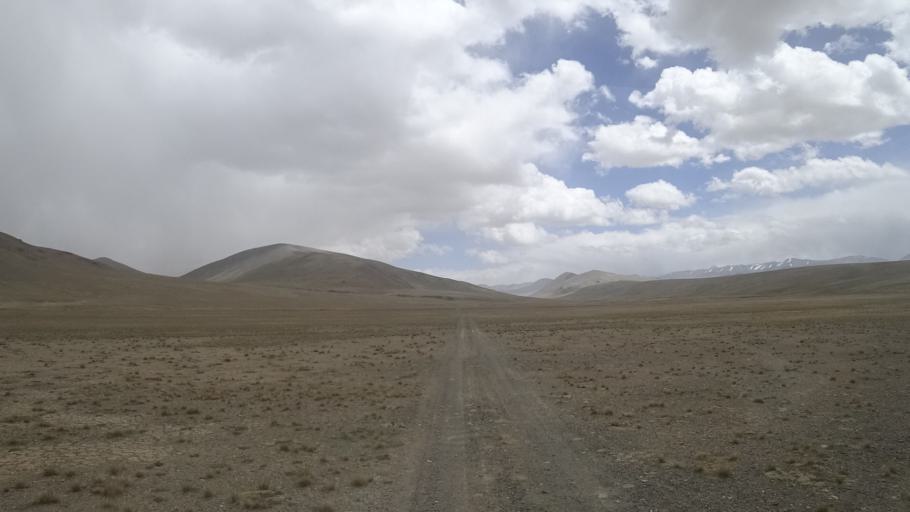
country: TJ
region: Gorno-Badakhshan
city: Murghob
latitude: 37.4905
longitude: 74.0260
